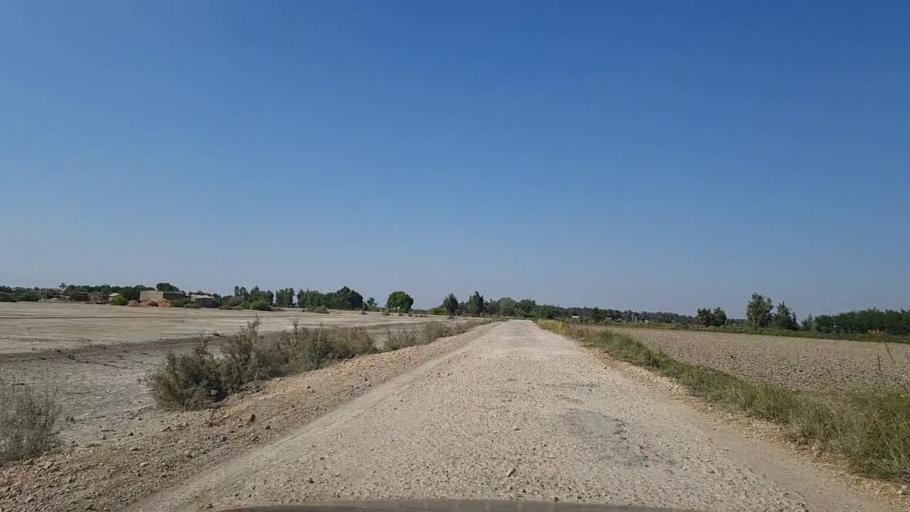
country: PK
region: Sindh
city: Mirpur Sakro
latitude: 24.6110
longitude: 67.7811
